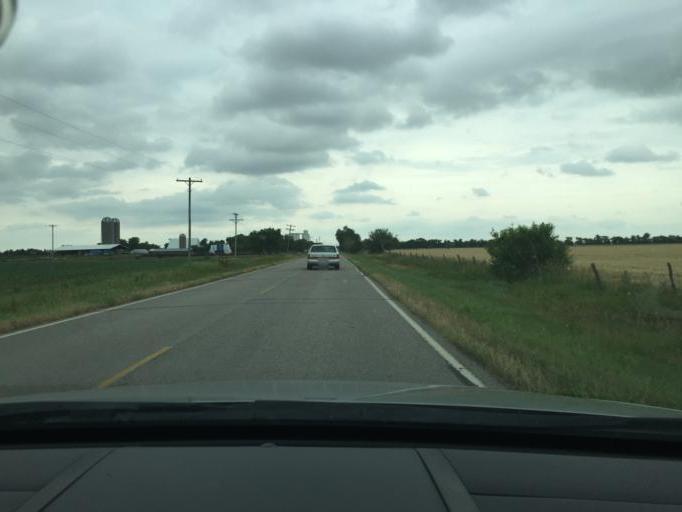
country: US
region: Kansas
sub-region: Reno County
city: South Hutchinson
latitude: 37.9943
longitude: -98.0138
